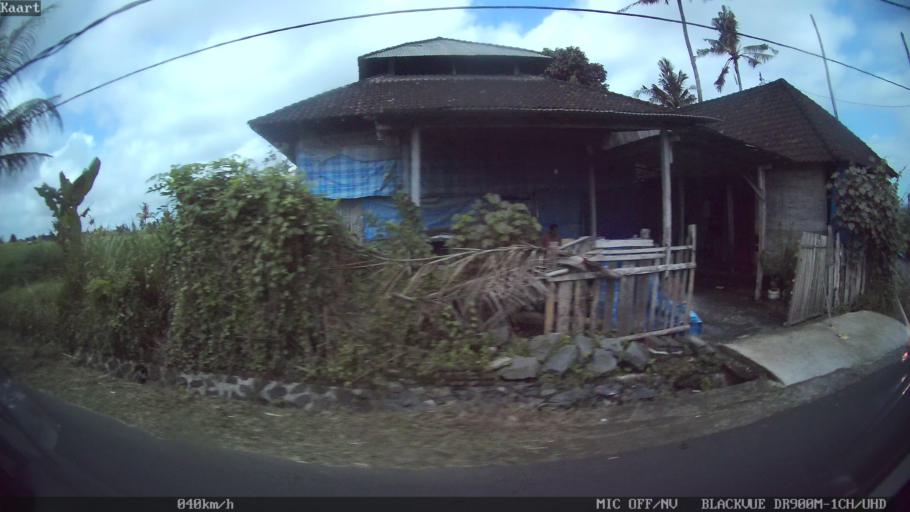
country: ID
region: Bali
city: Banjar Pesalakan
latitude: -8.5177
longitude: 115.3121
